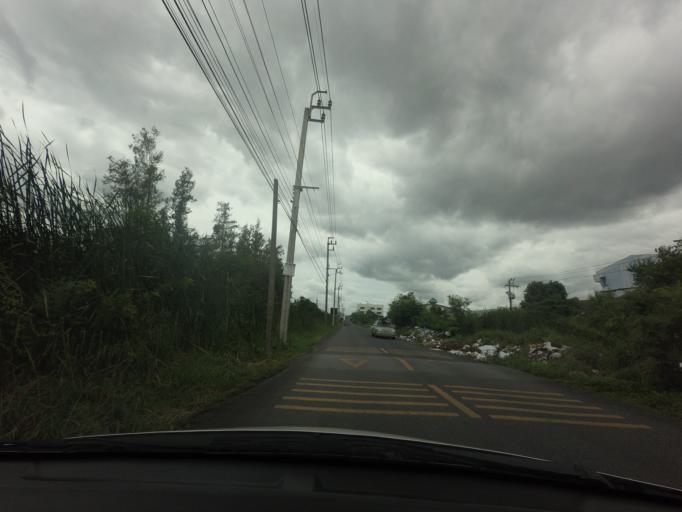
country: TH
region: Bangkok
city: Min Buri
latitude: 13.7753
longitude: 100.7486
